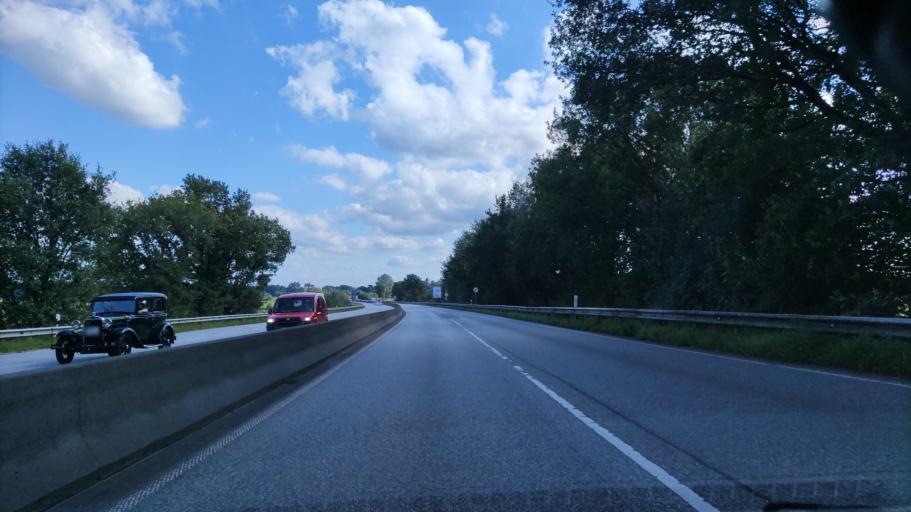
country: DE
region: Schleswig-Holstein
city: Fockbek
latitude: 54.3083
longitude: 9.6294
